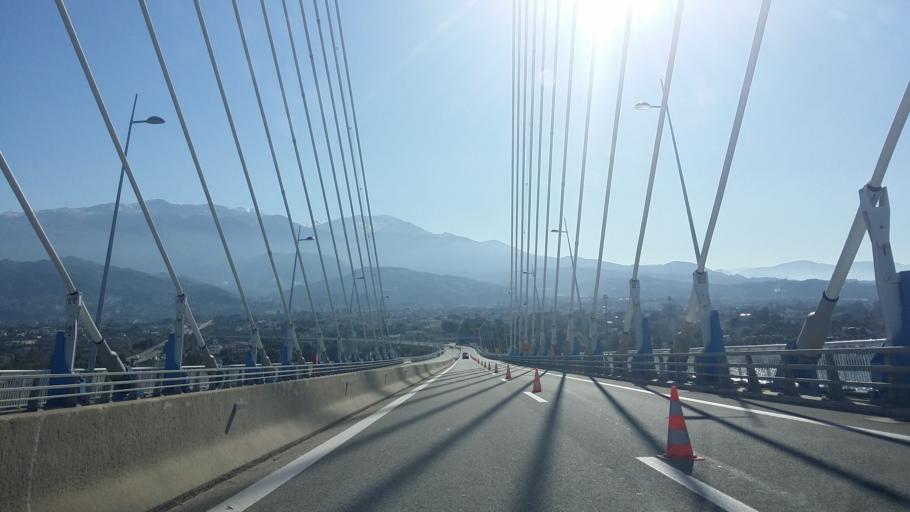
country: GR
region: West Greece
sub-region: Nomos Achaias
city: Rio
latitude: 38.3126
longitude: 21.7778
